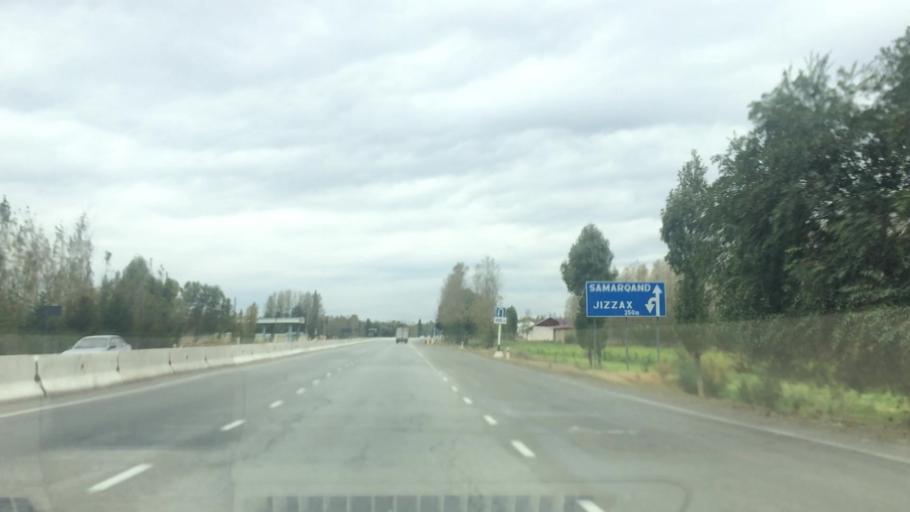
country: UZ
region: Jizzax
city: Jizzax
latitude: 39.9633
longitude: 67.5493
